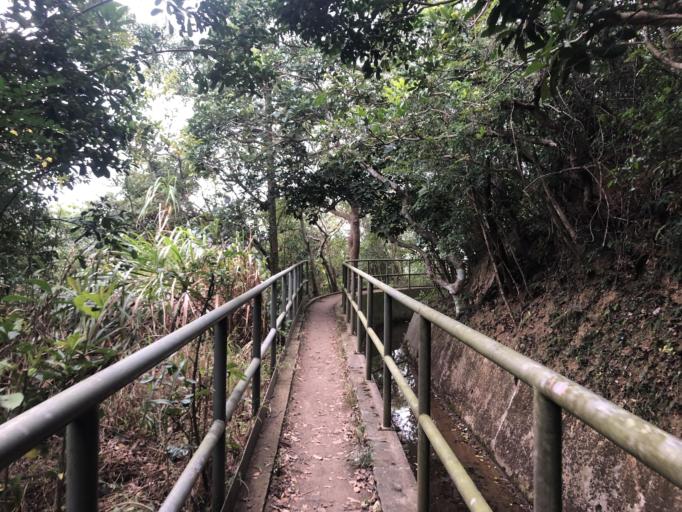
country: HK
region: Wanchai
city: Wan Chai
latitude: 22.2736
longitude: 114.2281
